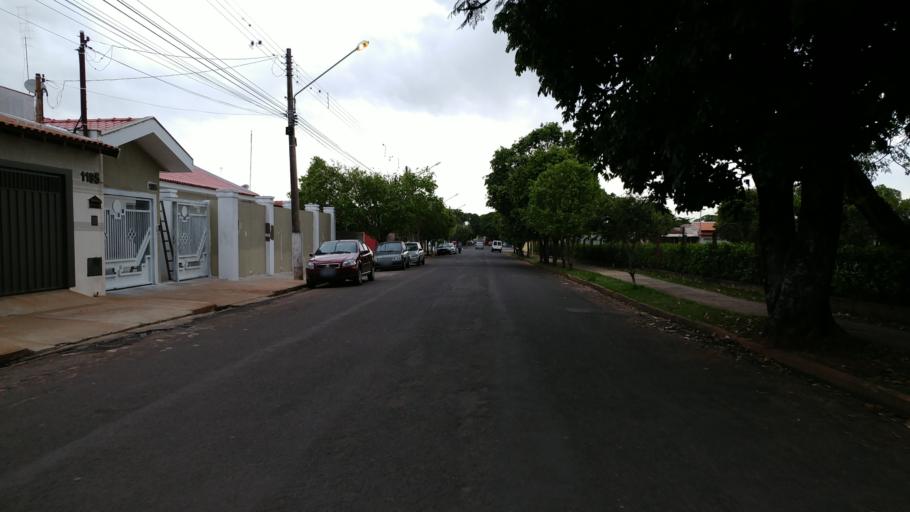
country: BR
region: Sao Paulo
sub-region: Paraguacu Paulista
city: Paraguacu Paulista
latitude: -22.4182
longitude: -50.5820
